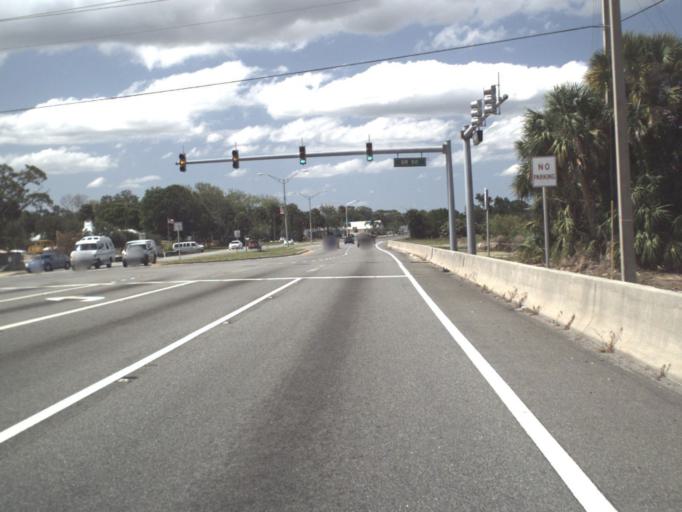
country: US
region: Florida
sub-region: Brevard County
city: Titusville
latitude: 28.5571
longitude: -80.7976
